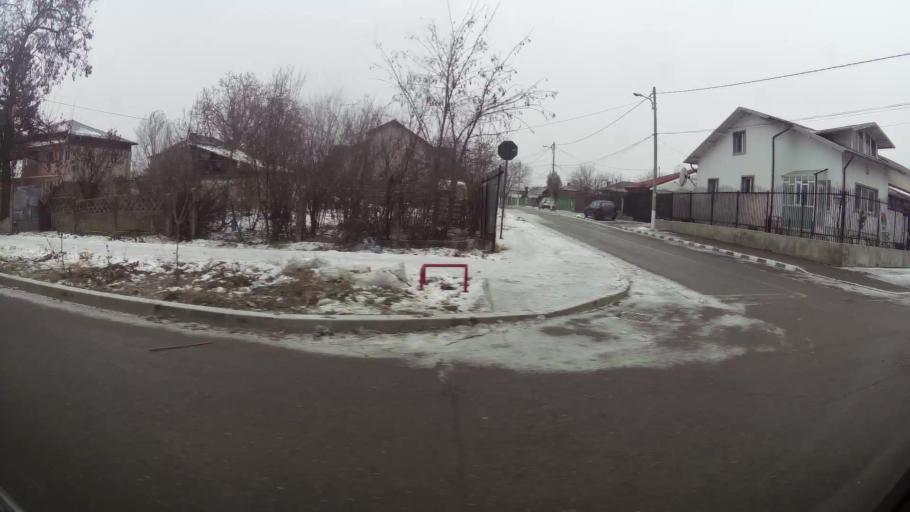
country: RO
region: Prahova
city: Ploiesti
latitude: 44.9490
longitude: 26.0490
